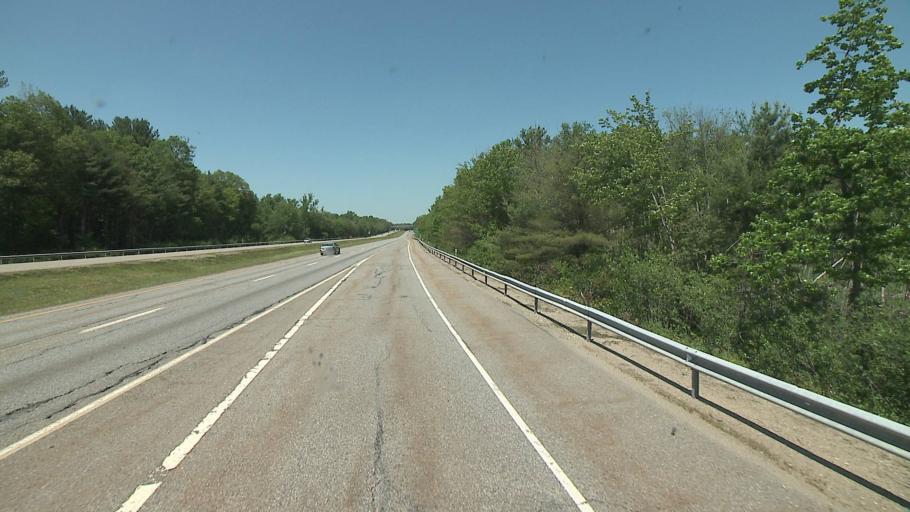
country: US
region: Connecticut
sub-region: Windham County
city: Putnam
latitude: 41.9124
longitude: -71.8900
